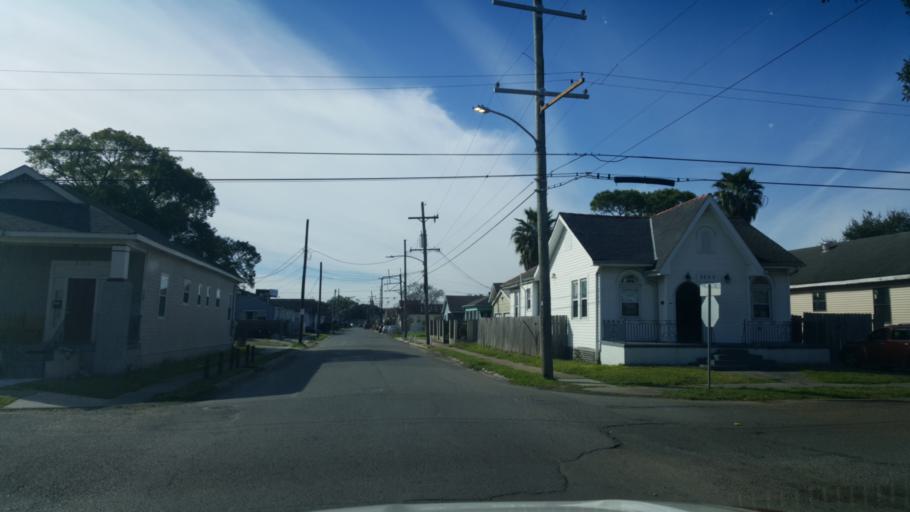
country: US
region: Louisiana
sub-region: Orleans Parish
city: New Orleans
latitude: 29.9800
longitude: -90.0529
